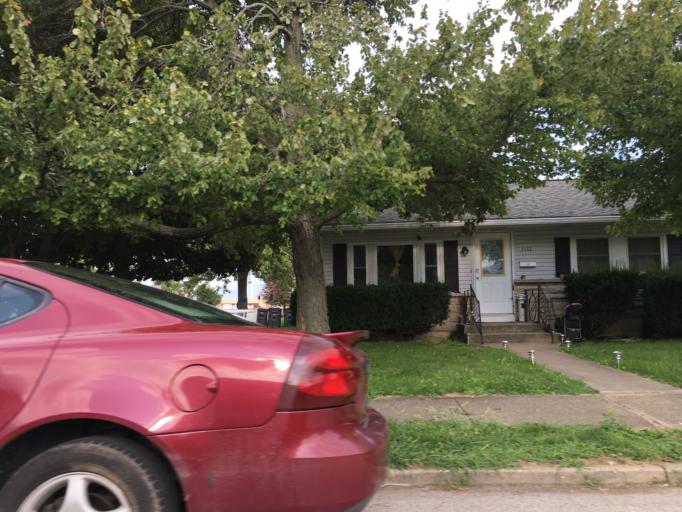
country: US
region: Indiana
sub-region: Howard County
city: Kokomo
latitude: 40.4632
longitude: -86.1258
